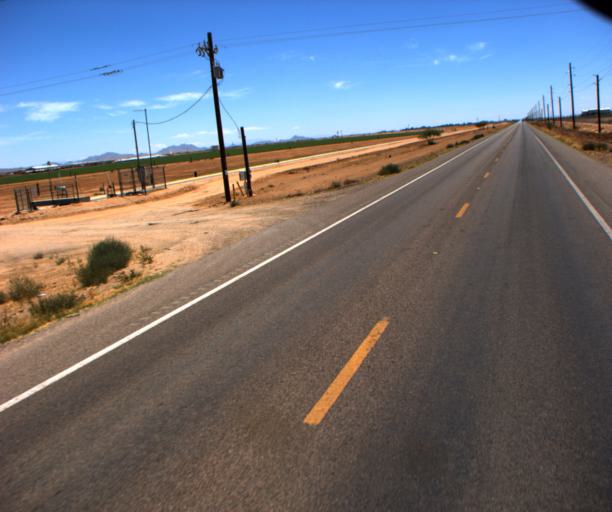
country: US
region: Arizona
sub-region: Pinal County
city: Casa Grande
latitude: 32.8794
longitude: -111.9210
